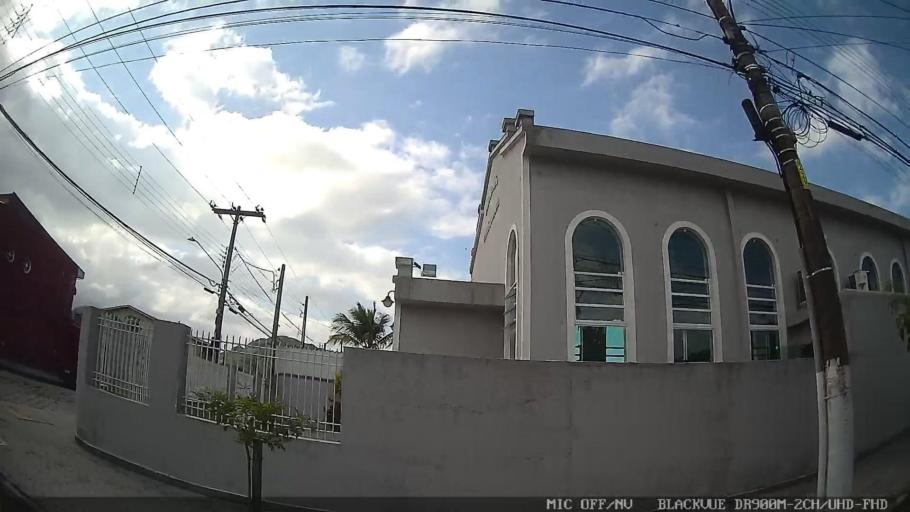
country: BR
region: Sao Paulo
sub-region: Guaruja
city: Guaruja
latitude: -23.9949
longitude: -46.2796
